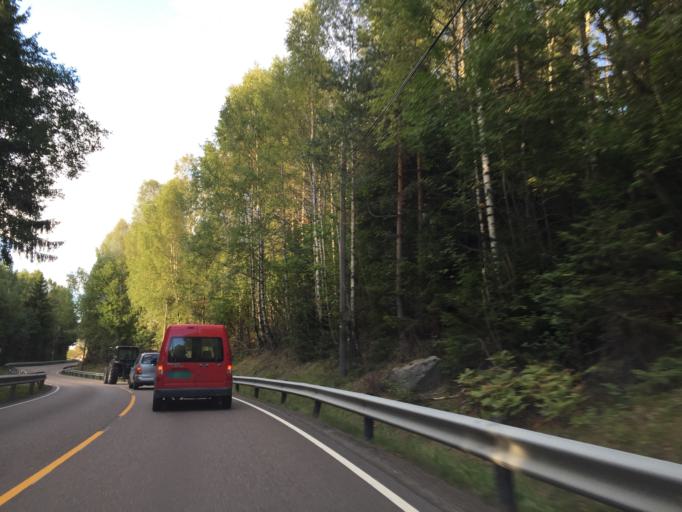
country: NO
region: Akershus
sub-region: Fet
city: Fetsund
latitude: 59.9117
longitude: 11.1840
